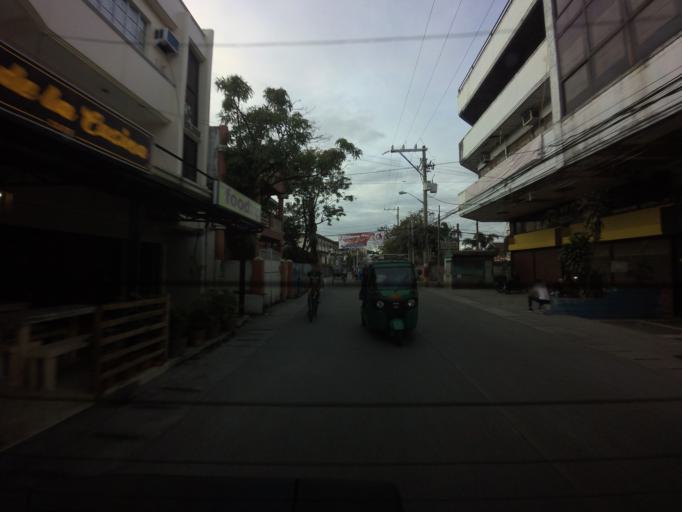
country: PH
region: Central Luzon
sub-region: Province of Bulacan
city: Obando
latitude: 14.7097
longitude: 120.9370
